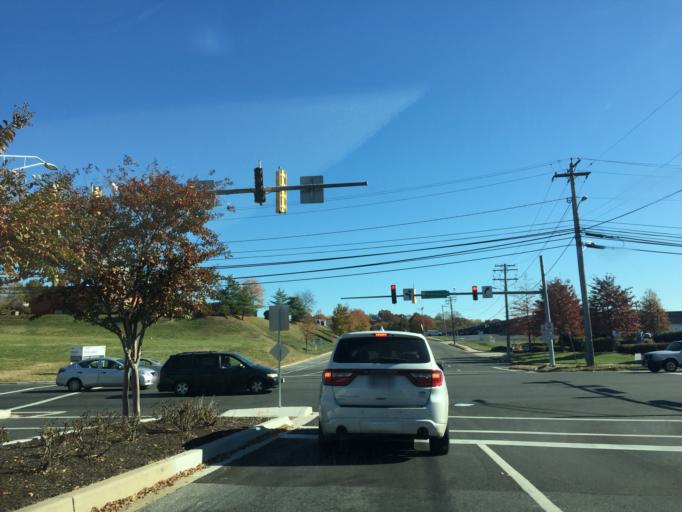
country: US
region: Maryland
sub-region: Baltimore County
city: Lansdowne
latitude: 39.2534
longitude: -76.6686
